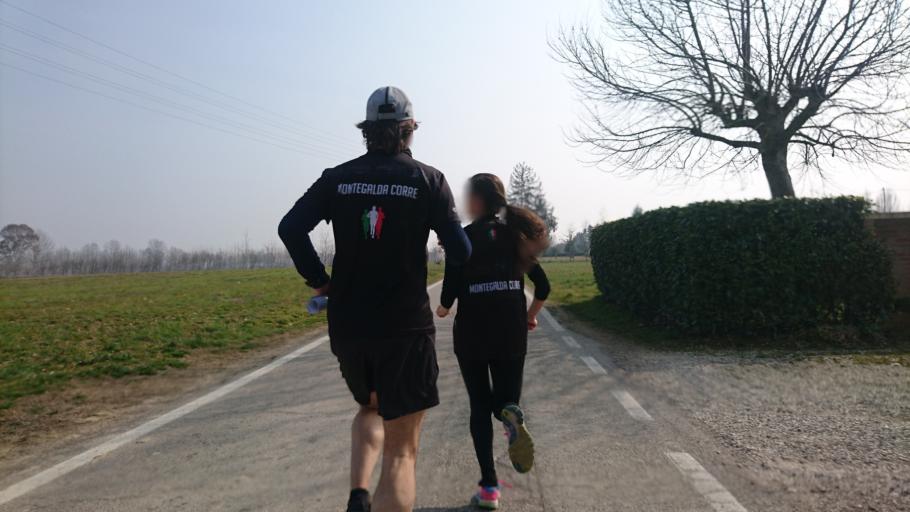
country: IT
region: Veneto
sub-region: Provincia di Vicenza
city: Montegalda
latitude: 45.4745
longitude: 11.6696
